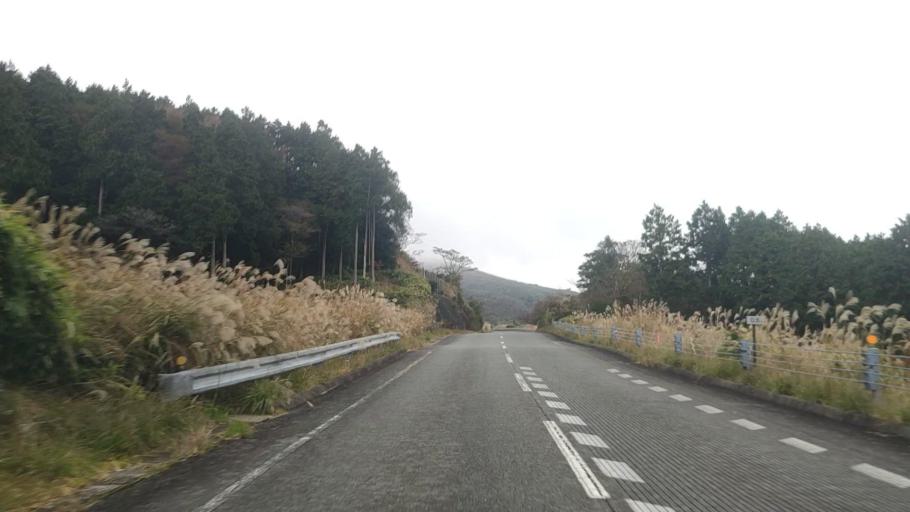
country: JP
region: Shizuoka
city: Heda
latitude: 34.8751
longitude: 138.8380
